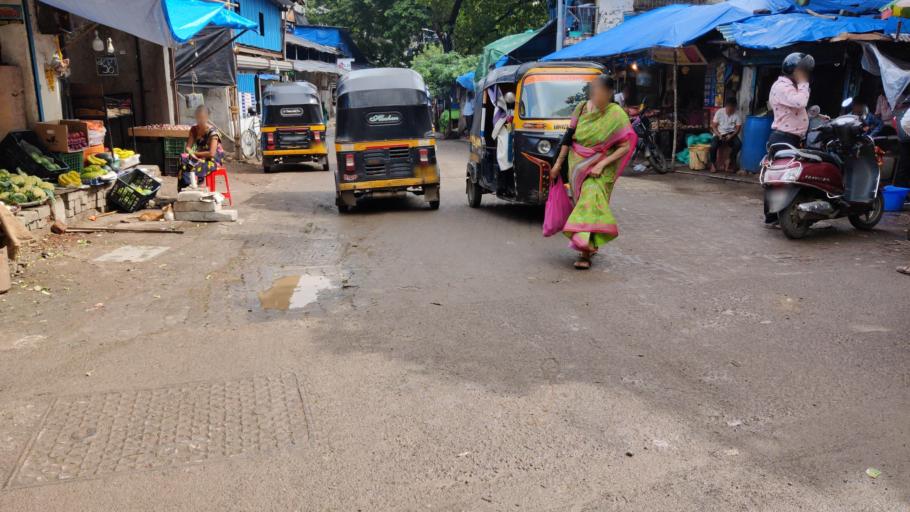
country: IN
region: Maharashtra
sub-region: Mumbai Suburban
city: Borivli
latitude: 19.2485
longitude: 72.8607
